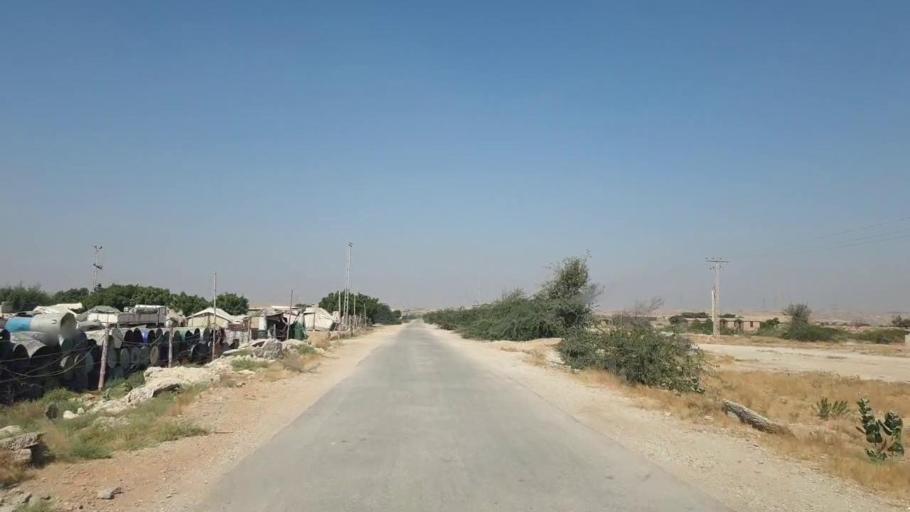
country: PK
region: Sindh
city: Thatta
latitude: 25.1821
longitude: 67.8061
